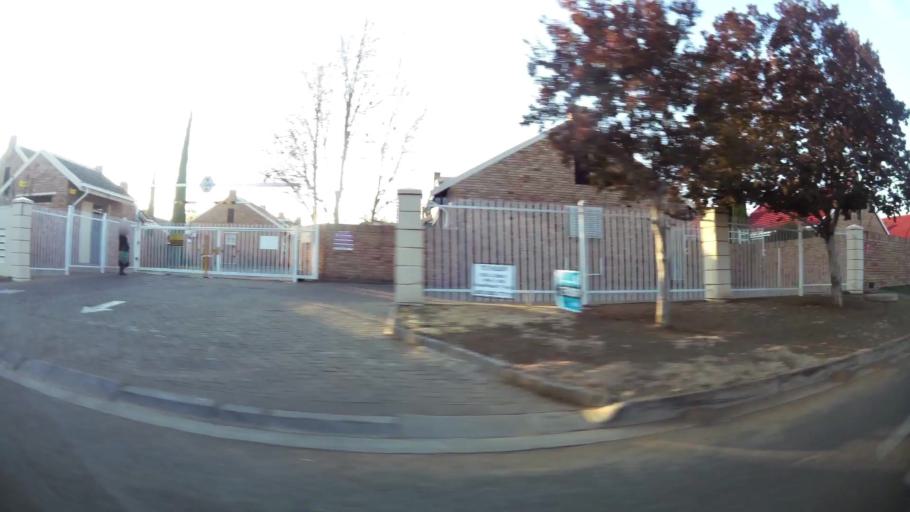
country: ZA
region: Orange Free State
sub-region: Mangaung Metropolitan Municipality
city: Bloemfontein
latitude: -29.0927
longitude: 26.1673
